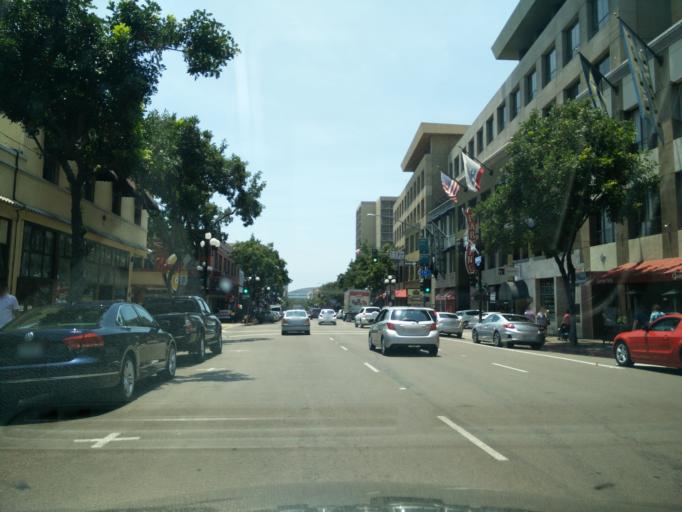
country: US
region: California
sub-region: San Diego County
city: San Diego
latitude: 32.7141
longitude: -117.1611
